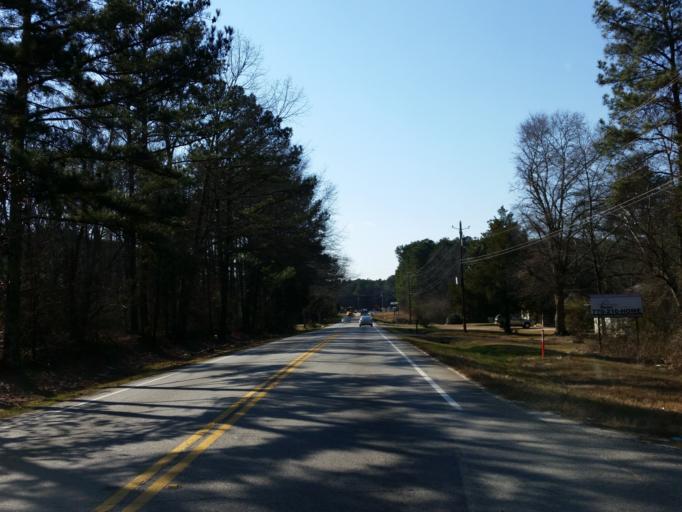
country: US
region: Georgia
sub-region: Clayton County
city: Lovejoy
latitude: 33.4250
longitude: -84.2807
